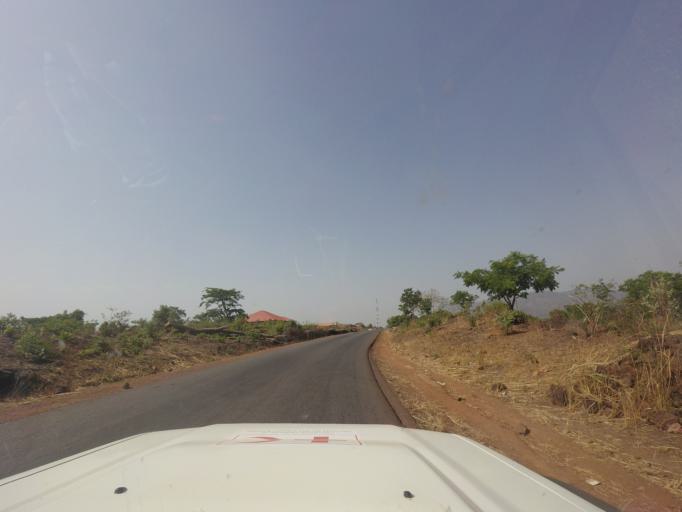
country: GN
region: Mamou
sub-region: Mamou Prefecture
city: Mamou
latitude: 10.2638
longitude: -12.4533
